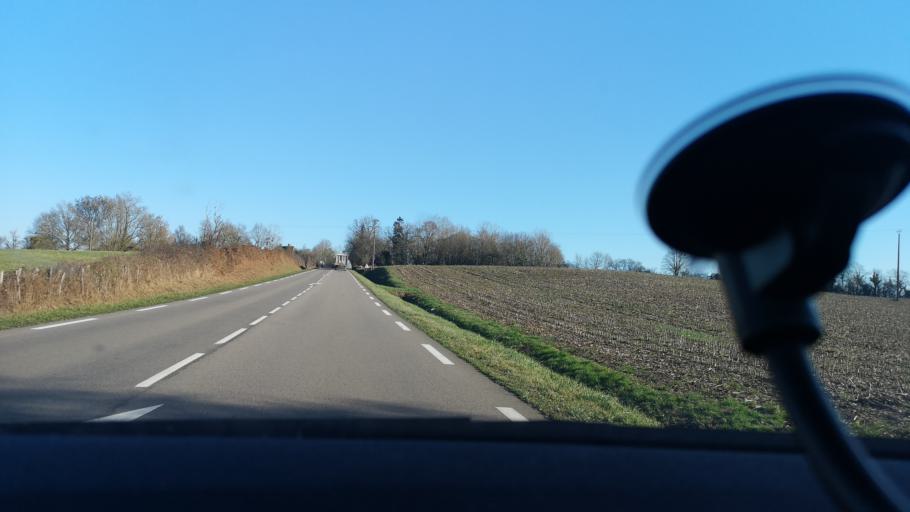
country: FR
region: Bourgogne
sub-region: Departement de Saone-et-Loire
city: Saint-Martin-en-Bresse
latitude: 46.7424
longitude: 5.1038
